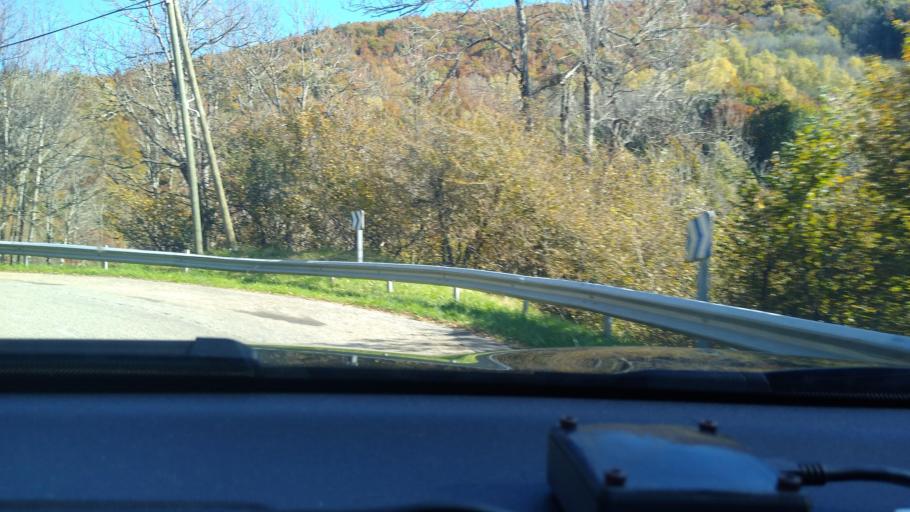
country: FR
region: Midi-Pyrenees
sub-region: Departement de l'Ariege
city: Ax-les-Thermes
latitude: 42.7212
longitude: 1.8809
